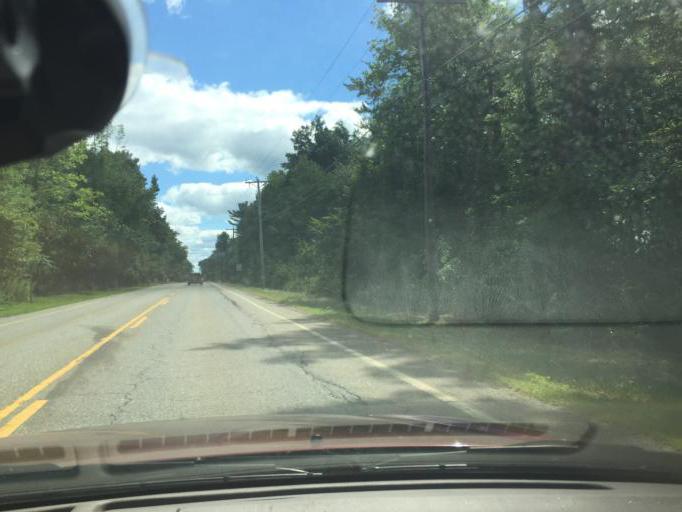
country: US
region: Connecticut
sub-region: Litchfield County
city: Litchfield
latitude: 41.8078
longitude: -73.2162
